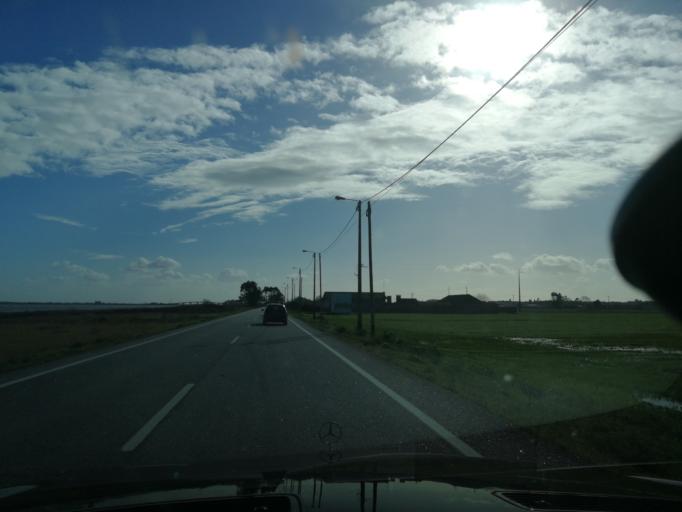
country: PT
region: Aveiro
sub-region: Estarreja
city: Pardilho
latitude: 40.8092
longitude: -8.6718
